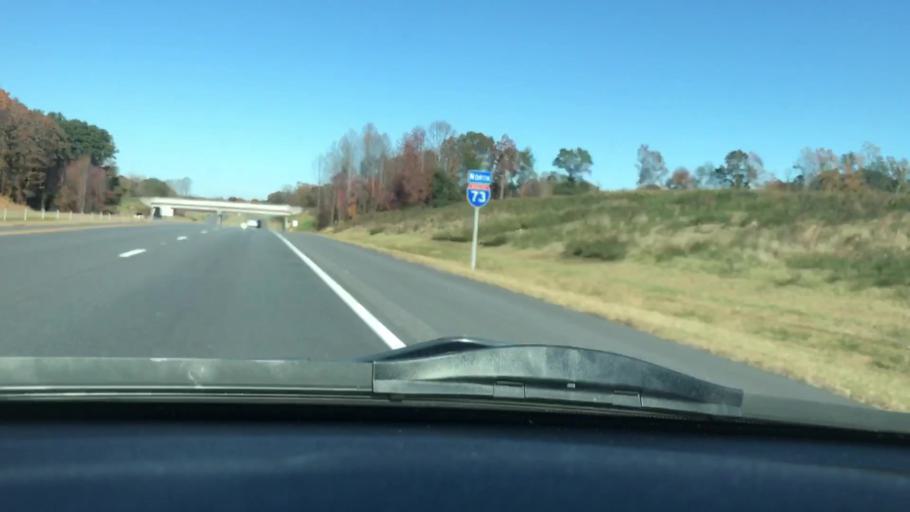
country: US
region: North Carolina
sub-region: Guilford County
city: Summerfield
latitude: 36.2106
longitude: -79.9213
